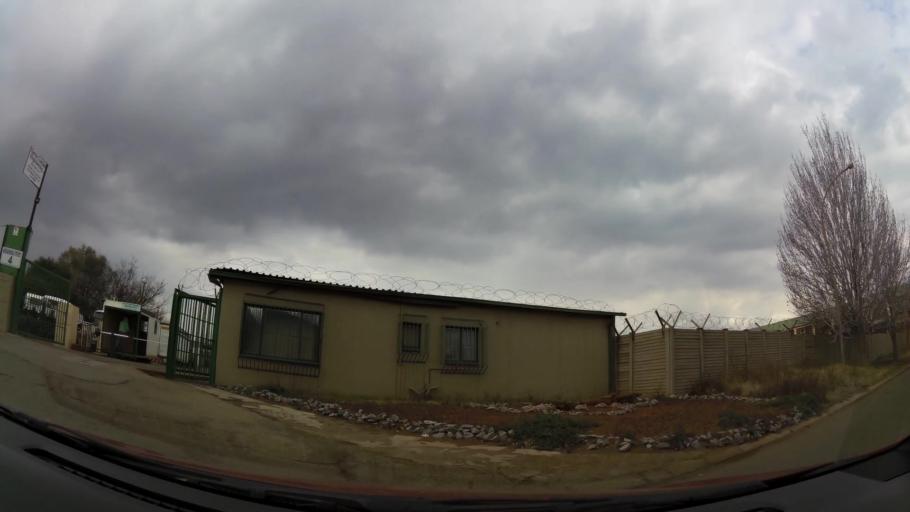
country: ZA
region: Gauteng
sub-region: Sedibeng District Municipality
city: Vanderbijlpark
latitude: -26.6889
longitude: 27.8074
